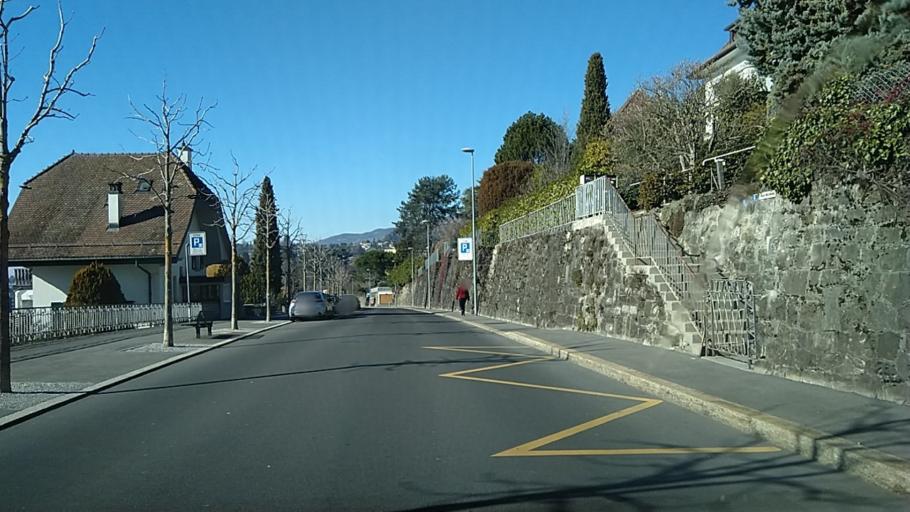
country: CH
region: Vaud
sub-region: Riviera-Pays-d'Enhaut District
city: Le Chatelard
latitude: 46.4415
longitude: 6.9044
